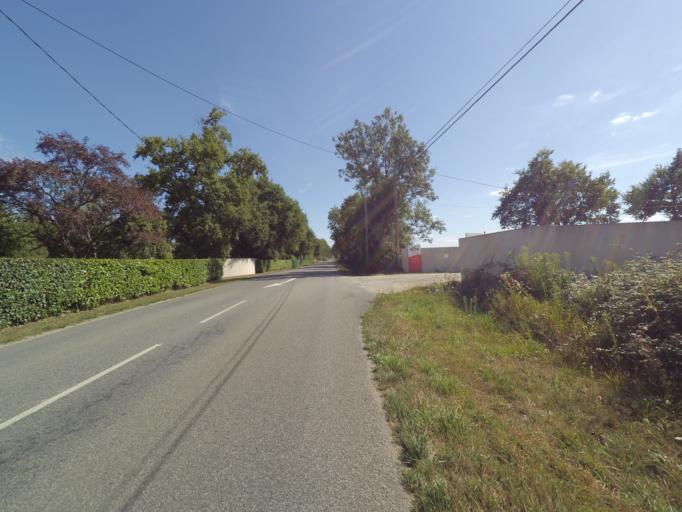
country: FR
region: Pays de la Loire
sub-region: Departement de la Loire-Atlantique
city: Vieillevigne
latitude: 46.9626
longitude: -1.4242
